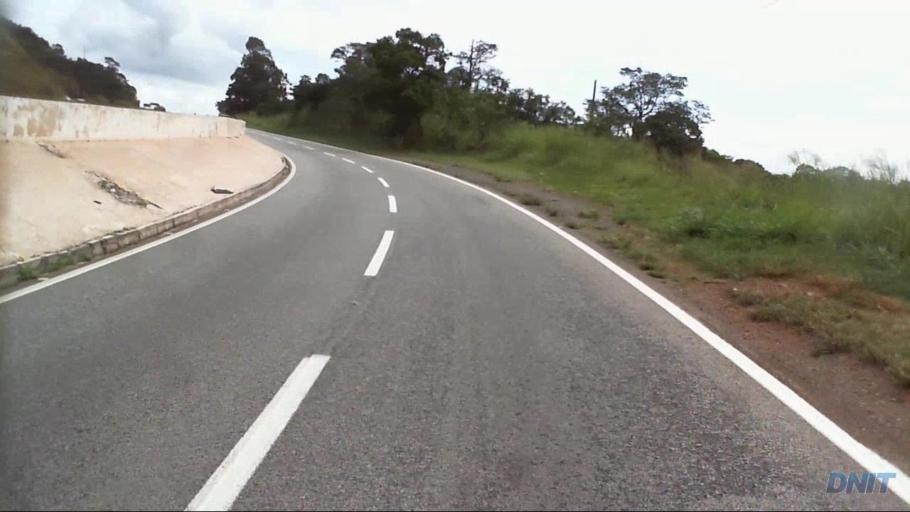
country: BR
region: Minas Gerais
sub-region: Caete
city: Caete
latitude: -19.7873
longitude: -43.6827
